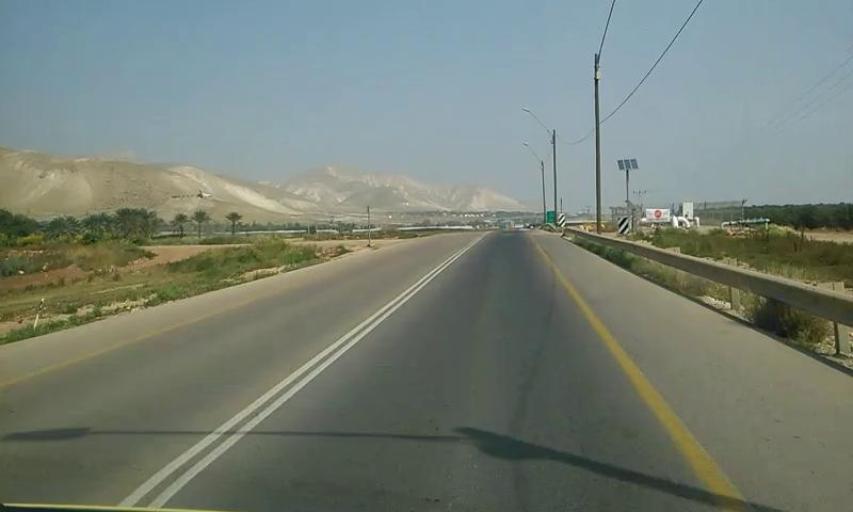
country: PS
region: West Bank
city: Al Fasayil
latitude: 32.0432
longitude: 35.4608
